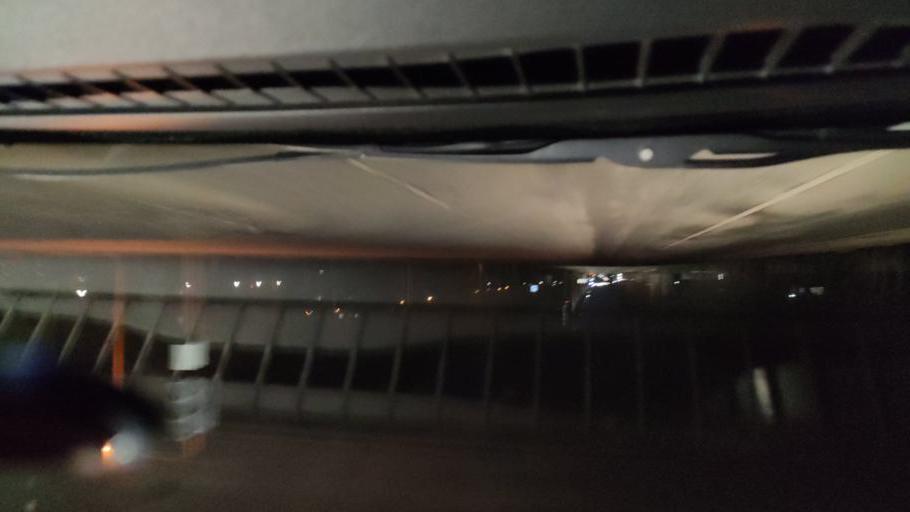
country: RU
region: Bashkortostan
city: Sterlitamak
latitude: 53.6414
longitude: 55.8990
